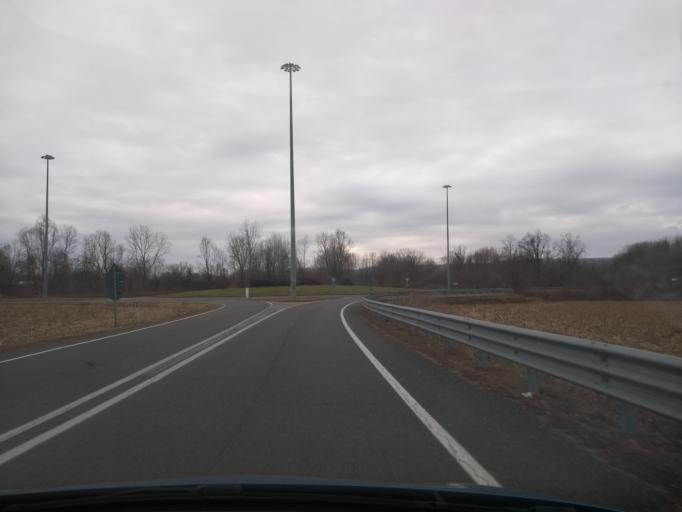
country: IT
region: Piedmont
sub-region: Provincia di Torino
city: Loranze
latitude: 45.4367
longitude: 7.8226
